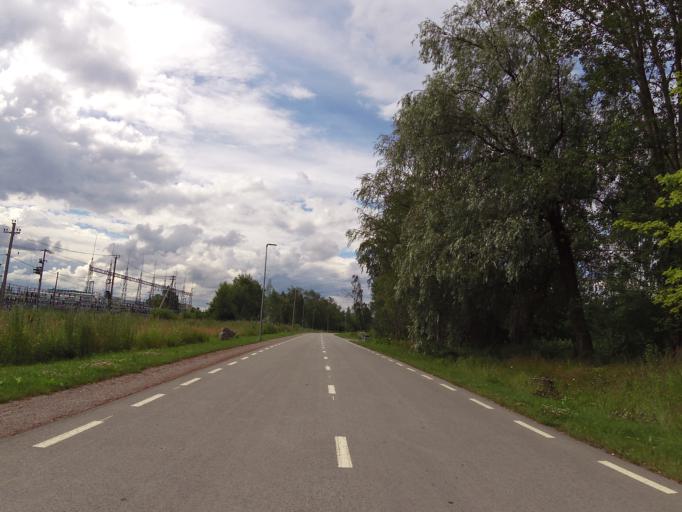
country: EE
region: Harju
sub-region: Tallinna linn
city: Tallinn
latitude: 59.4180
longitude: 24.6719
